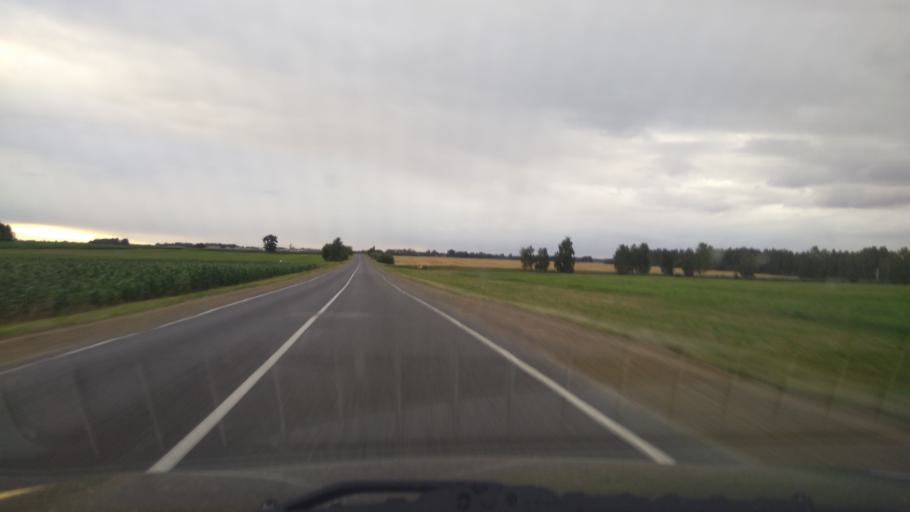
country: BY
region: Brest
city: Byaroza
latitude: 52.4356
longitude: 24.9799
